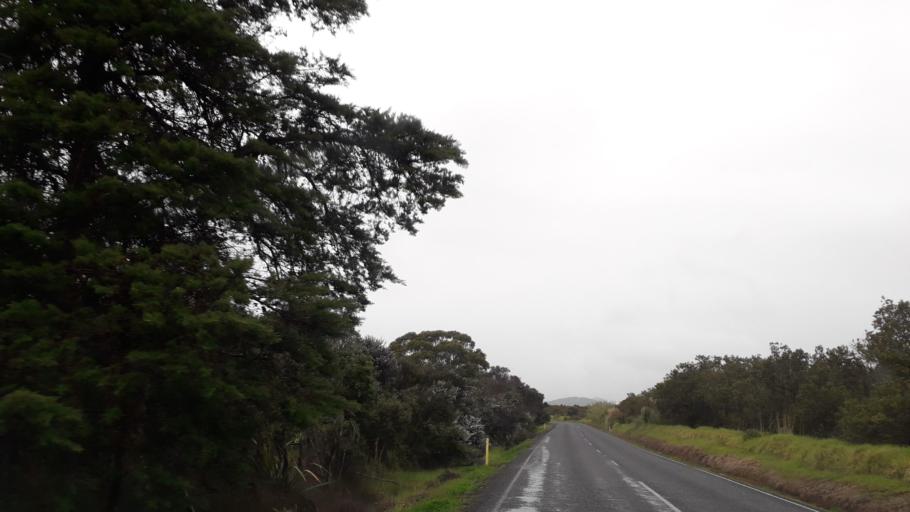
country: NZ
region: Northland
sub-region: Far North District
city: Kaitaia
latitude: -35.3717
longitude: 173.5022
